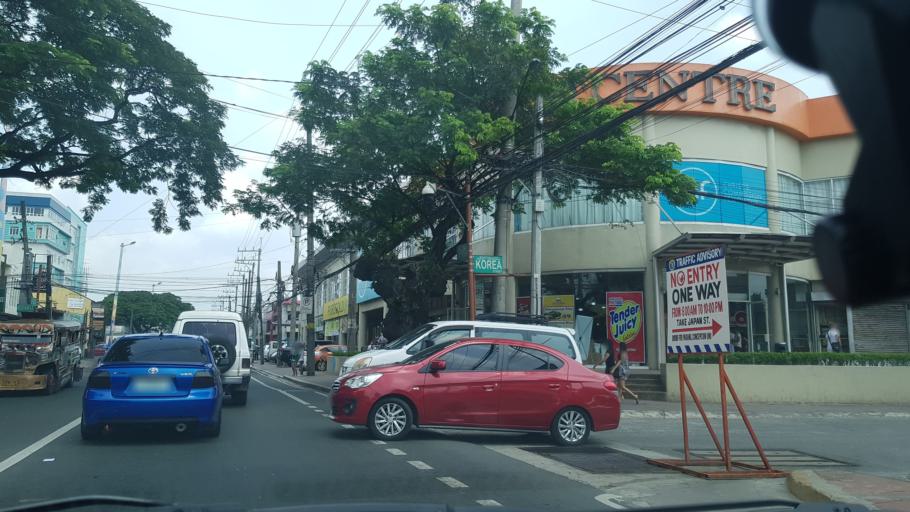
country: PH
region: Calabarzon
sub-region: Province of Rizal
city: San Mateo
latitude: 14.6691
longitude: 121.1081
